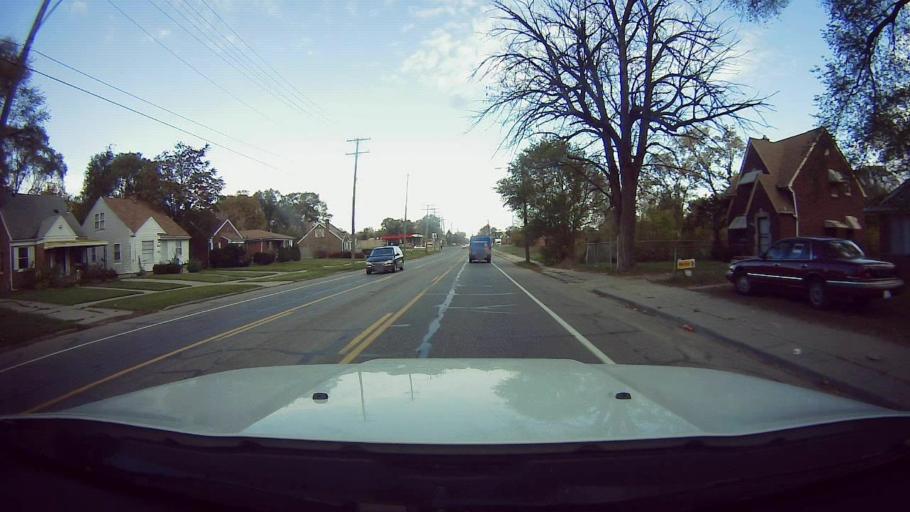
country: US
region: Michigan
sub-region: Wayne County
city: Dearborn
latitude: 42.3639
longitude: -83.1775
